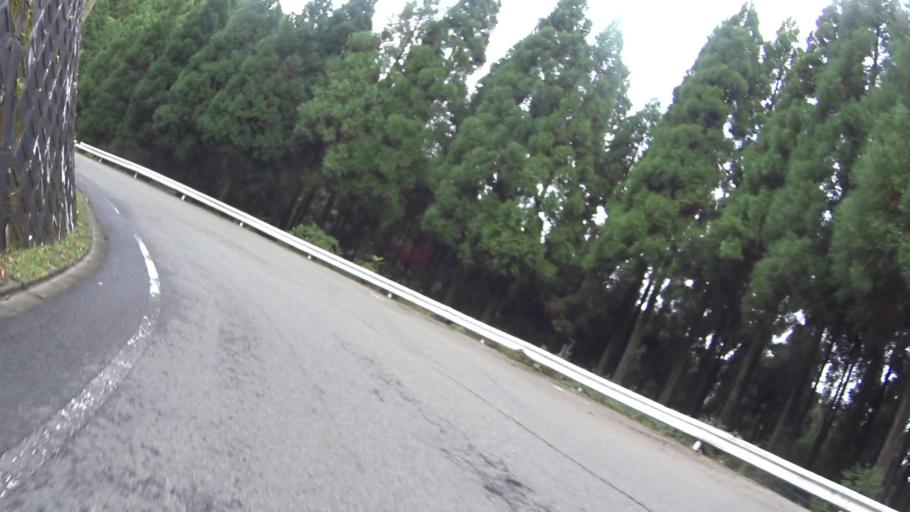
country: JP
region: Kyoto
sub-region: Kyoto-shi
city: Kamigyo-ku
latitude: 35.1593
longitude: 135.7807
